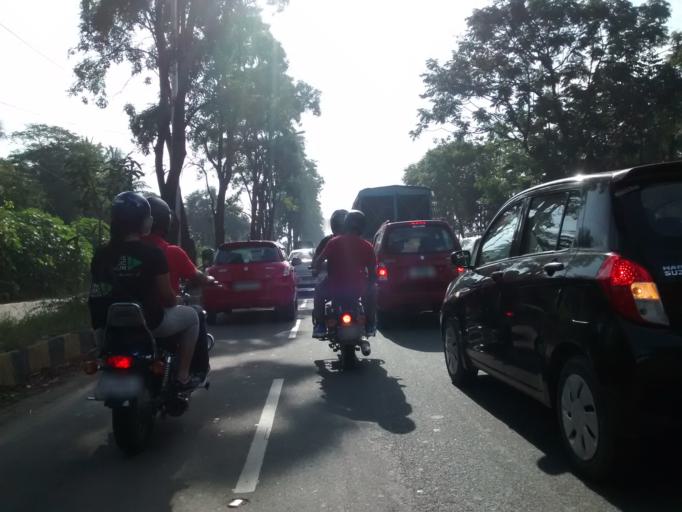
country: IN
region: Karnataka
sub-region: Bangalore Urban
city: Yelahanka
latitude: 13.0436
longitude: 77.6022
